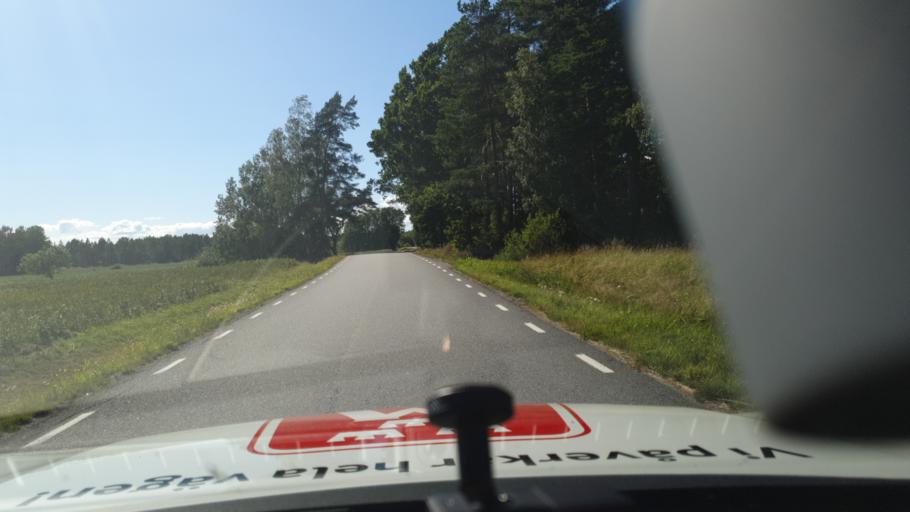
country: SE
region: Vaermland
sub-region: Saffle Kommun
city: Saeffle
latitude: 58.9369
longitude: 13.1823
